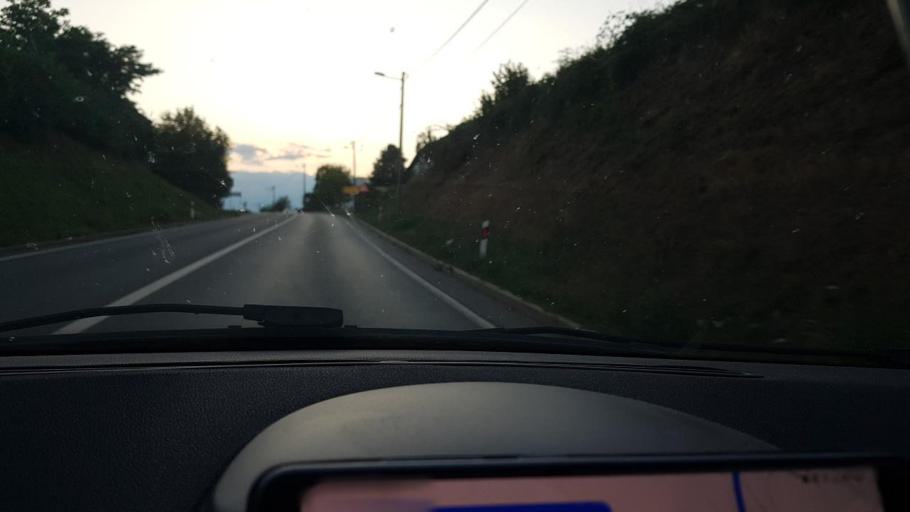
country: HR
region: Bjelovarsko-Bilogorska
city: Zdralovi
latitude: 45.8755
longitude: 16.8814
